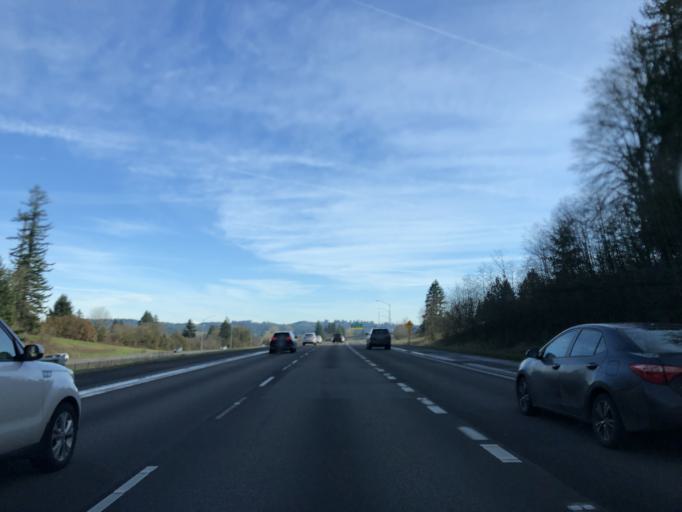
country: US
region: Oregon
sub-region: Clackamas County
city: Stafford
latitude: 45.3724
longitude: -122.7163
